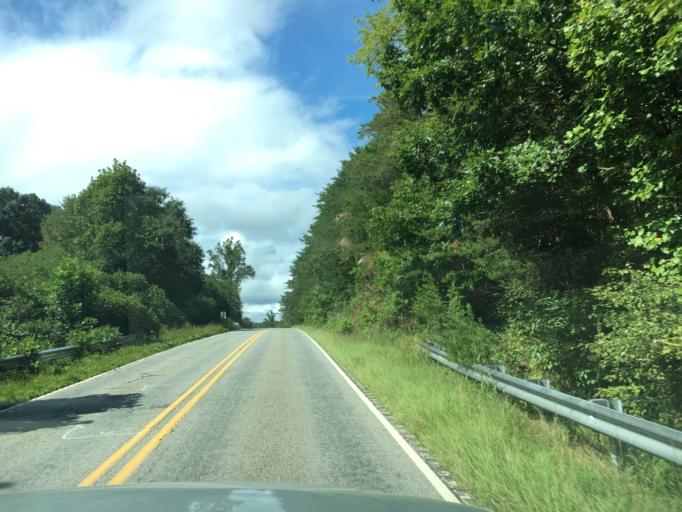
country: US
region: North Carolina
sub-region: Rutherford County
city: Lake Lure
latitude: 35.3821
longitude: -82.1913
